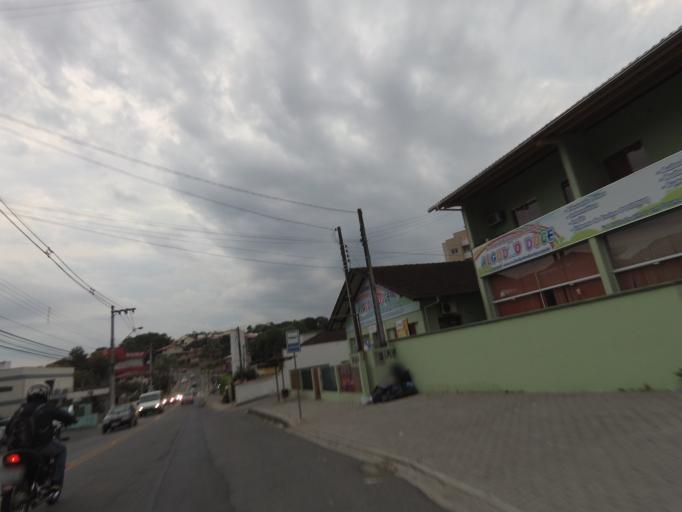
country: BR
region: Santa Catarina
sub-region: Blumenau
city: Blumenau
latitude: -26.8791
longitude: -49.0604
